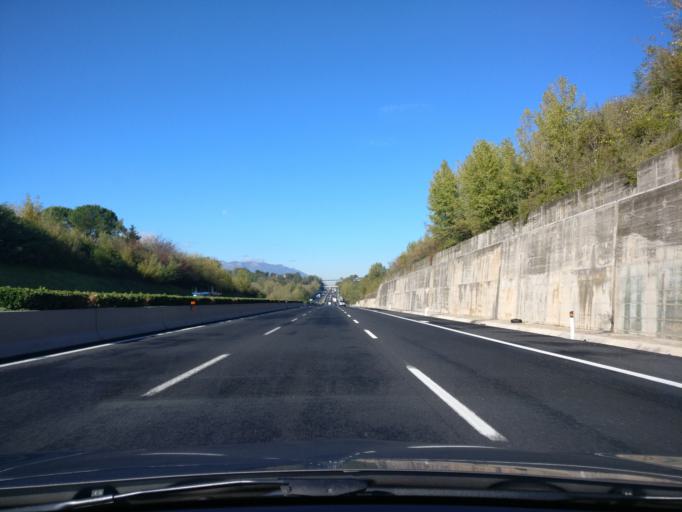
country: IT
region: Latium
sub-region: Provincia di Frosinone
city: Pofi
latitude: 41.5651
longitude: 13.3958
